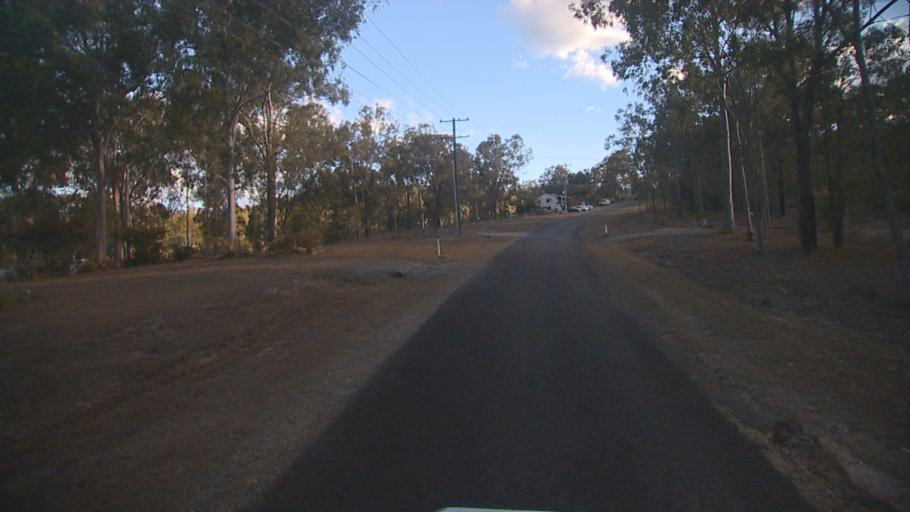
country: AU
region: Queensland
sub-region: Logan
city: Cedar Vale
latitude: -27.8477
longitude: 153.0820
